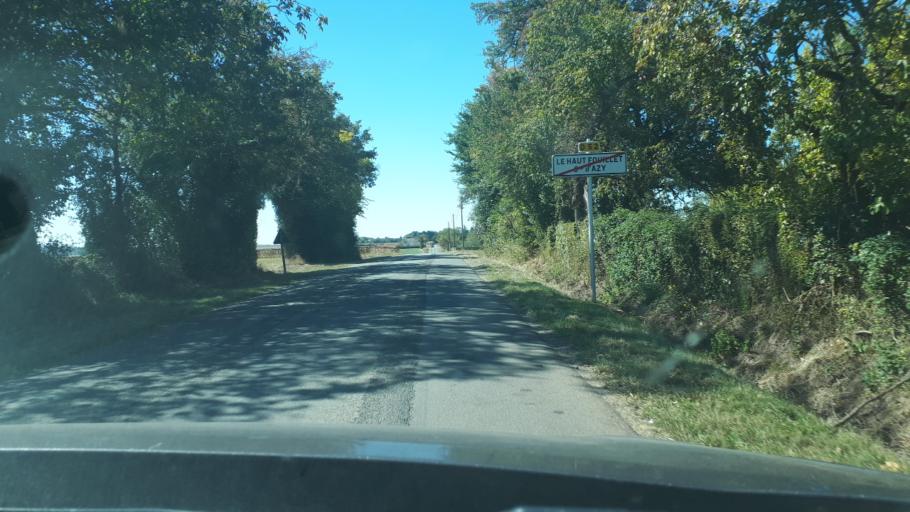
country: FR
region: Centre
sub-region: Departement du Cher
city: Baugy
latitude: 47.2027
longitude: 2.7330
